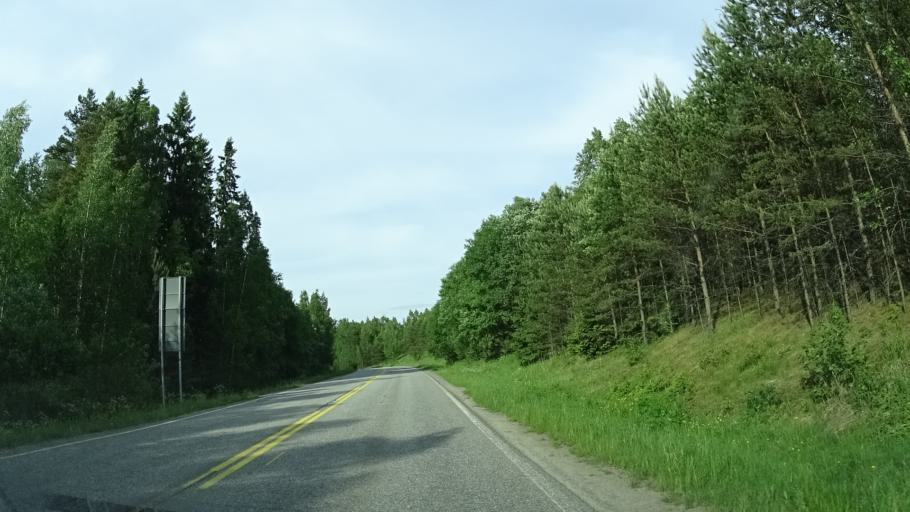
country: FI
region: Uusimaa
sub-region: Helsinki
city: Kirkkonummi
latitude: 60.1072
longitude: 24.4808
